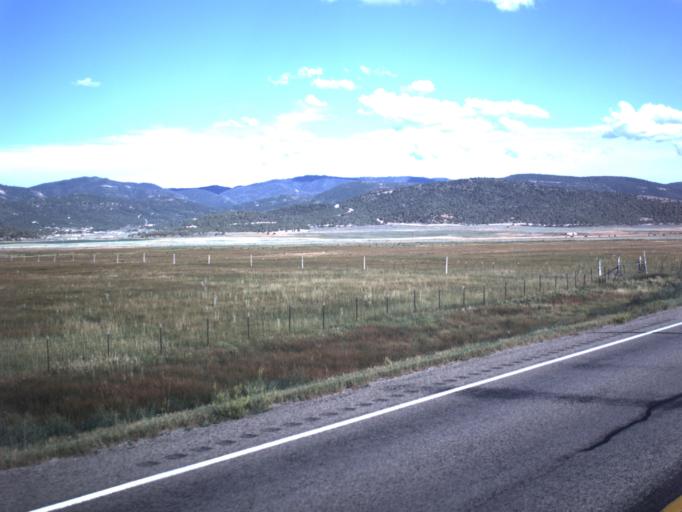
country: US
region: Utah
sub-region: Sanpete County
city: Fairview
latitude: 39.7926
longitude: -111.4976
